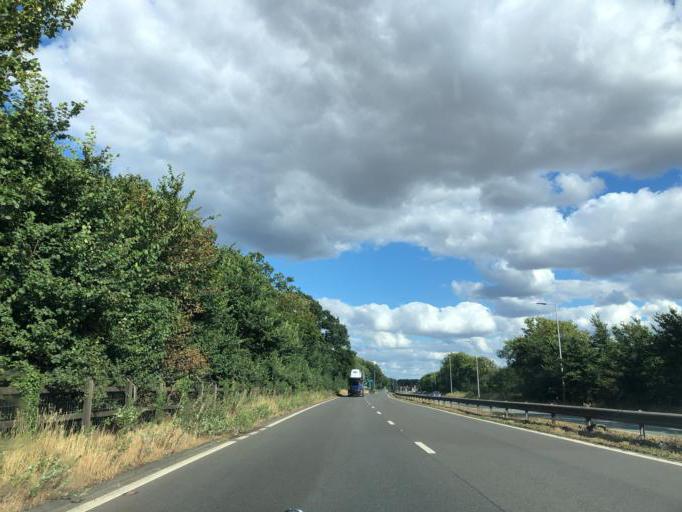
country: GB
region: England
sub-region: Warwickshire
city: Long Lawford
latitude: 52.3472
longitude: -1.3483
